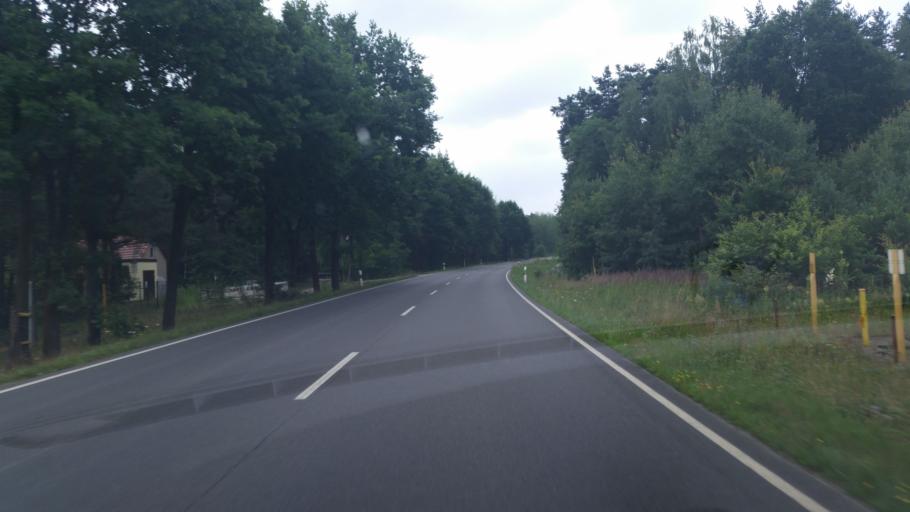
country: DE
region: Brandenburg
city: Senftenberg
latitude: 51.4817
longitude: 14.0697
